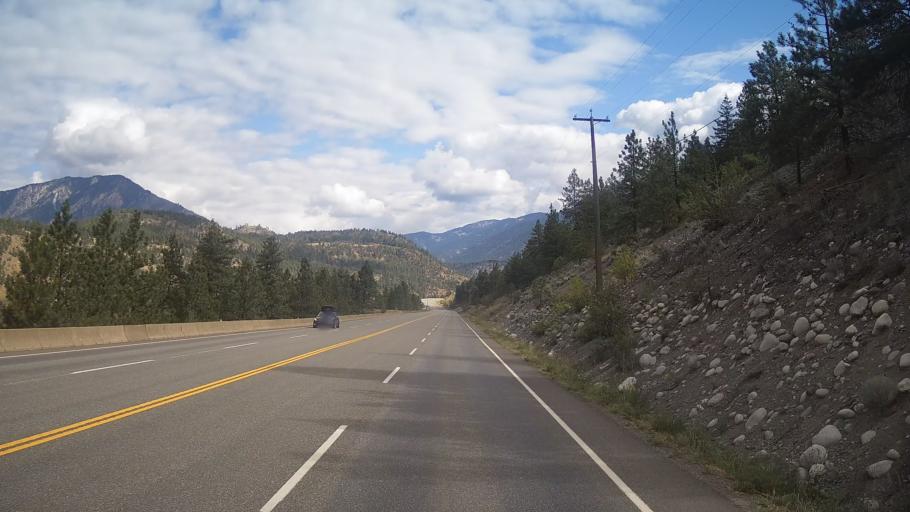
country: CA
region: British Columbia
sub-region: Thompson-Nicola Regional District
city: Ashcroft
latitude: 50.2350
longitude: -121.5765
